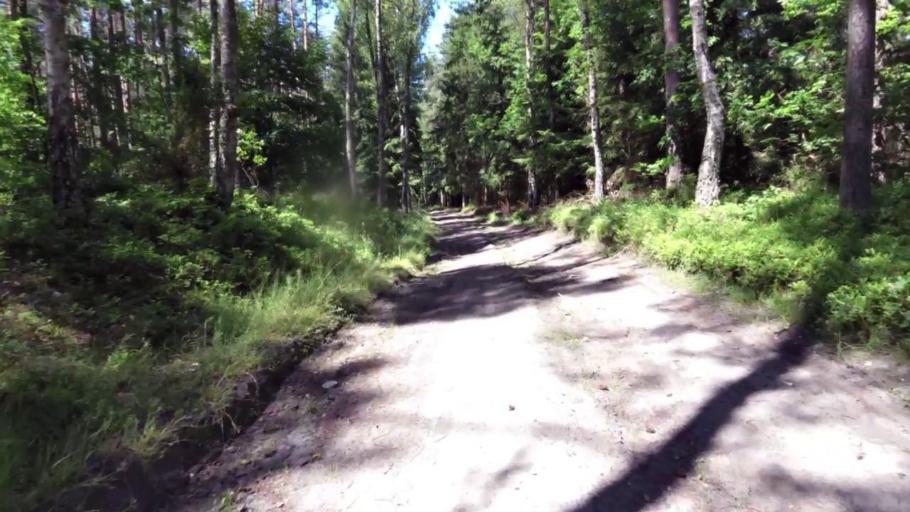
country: PL
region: West Pomeranian Voivodeship
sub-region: Powiat bialogardzki
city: Bialogard
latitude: 53.9558
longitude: 16.0977
